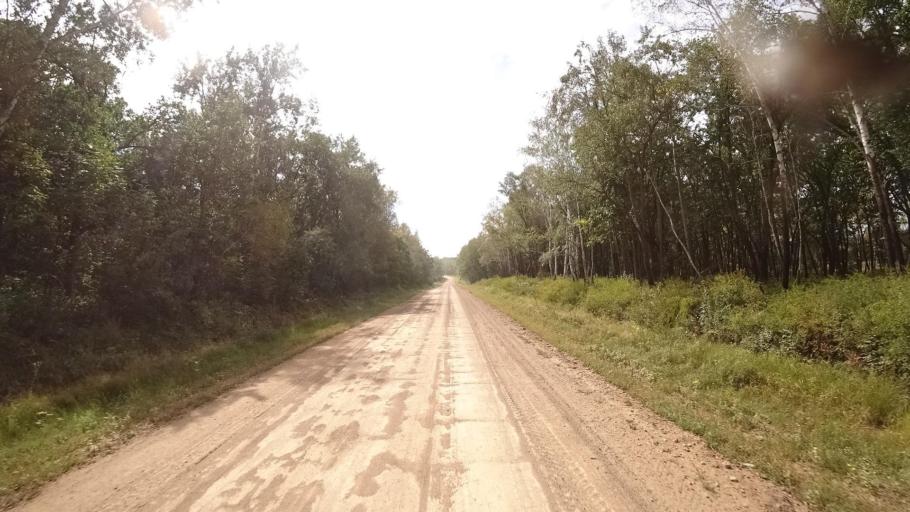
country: RU
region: Primorskiy
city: Yakovlevka
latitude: 44.5564
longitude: 133.5868
